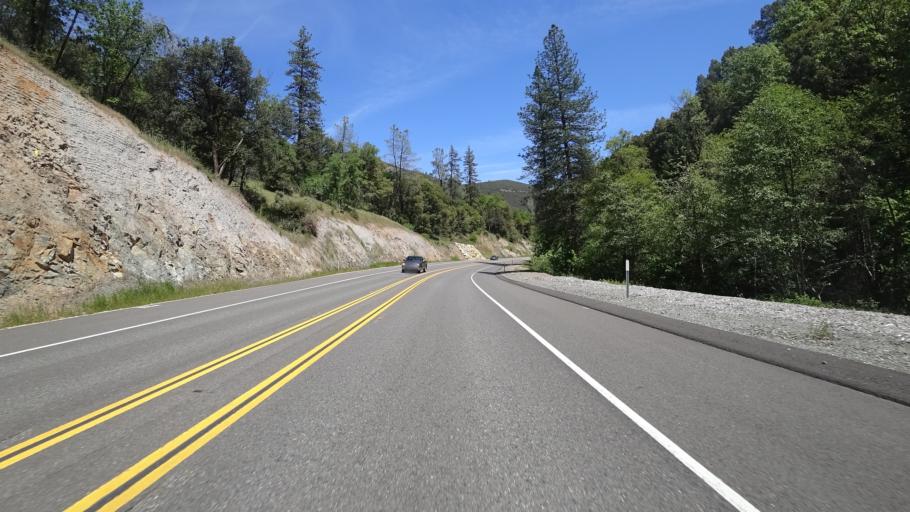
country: US
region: California
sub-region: Trinity County
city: Lewiston
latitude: 40.6735
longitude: -122.6723
